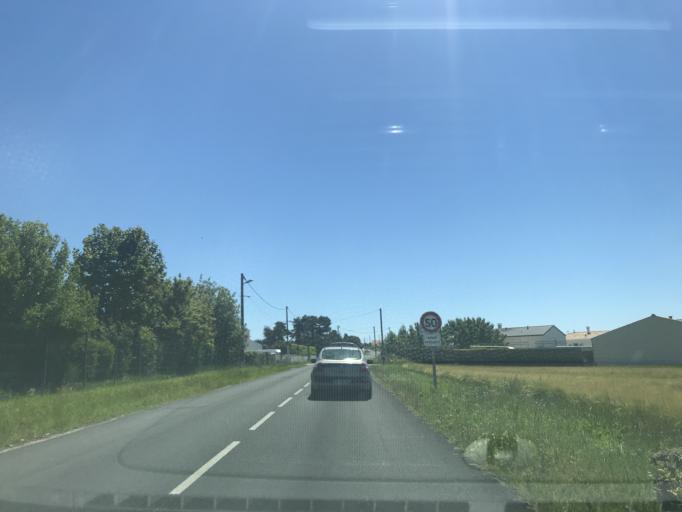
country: FR
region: Poitou-Charentes
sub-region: Departement de la Charente-Maritime
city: Meschers-sur-Gironde
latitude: 45.5791
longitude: -0.9596
